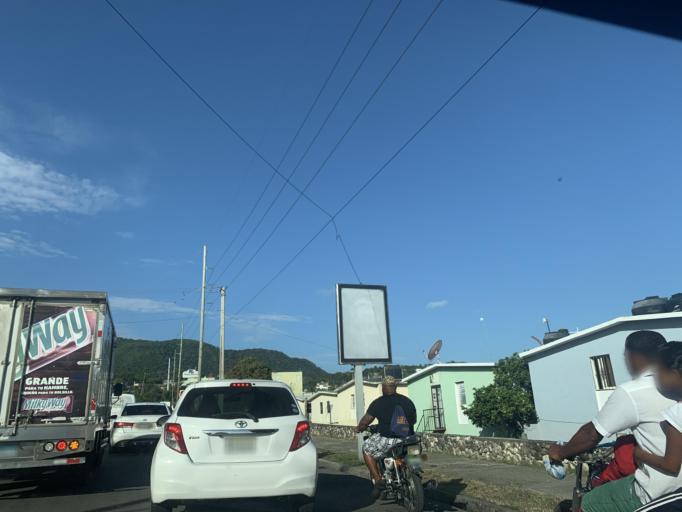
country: DO
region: Puerto Plata
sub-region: Puerto Plata
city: Puerto Plata
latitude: 19.7937
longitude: -70.7035
